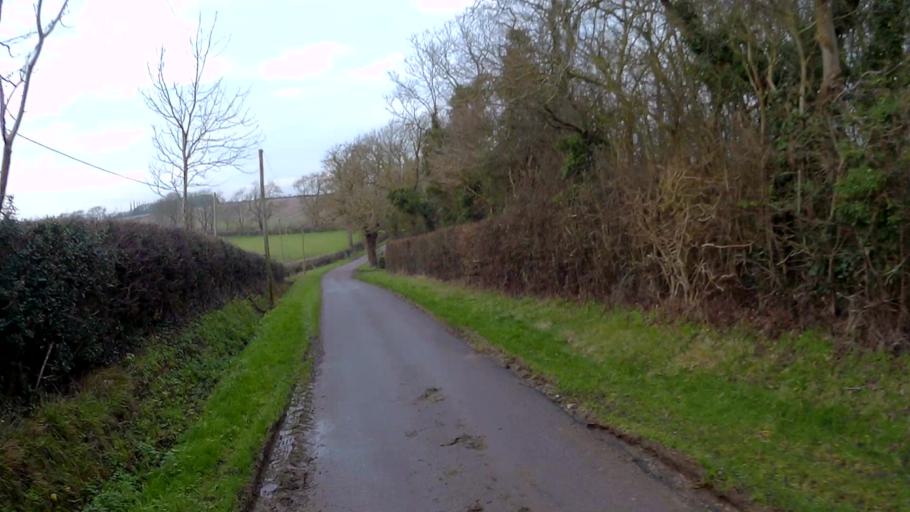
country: GB
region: England
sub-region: Lincolnshire
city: Bourne
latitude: 52.8262
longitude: -0.4604
